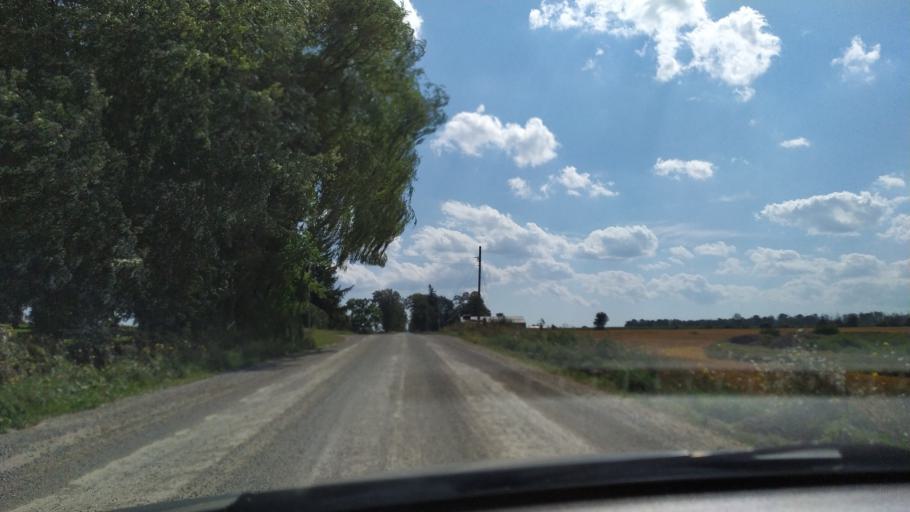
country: CA
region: Ontario
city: Stratford
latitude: 43.2878
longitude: -80.9302
